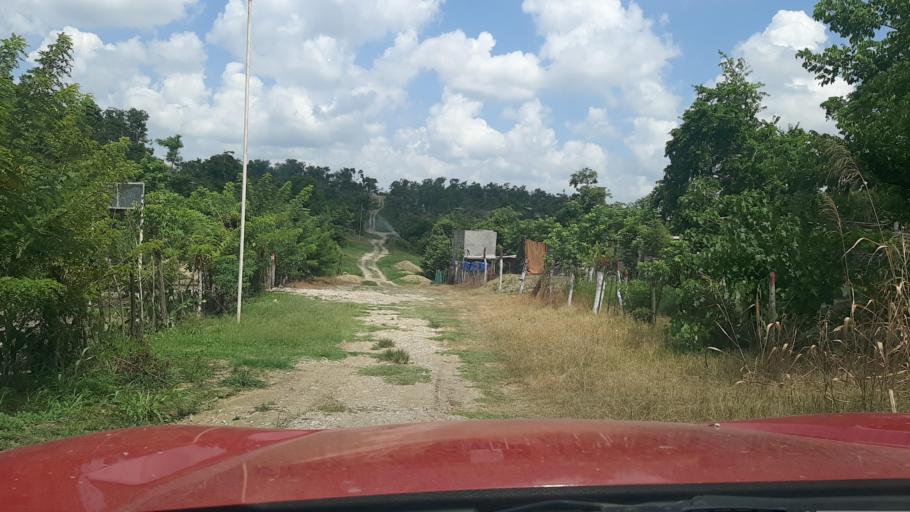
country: MX
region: Veracruz
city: Coatzintla
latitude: 20.5030
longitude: -97.4573
